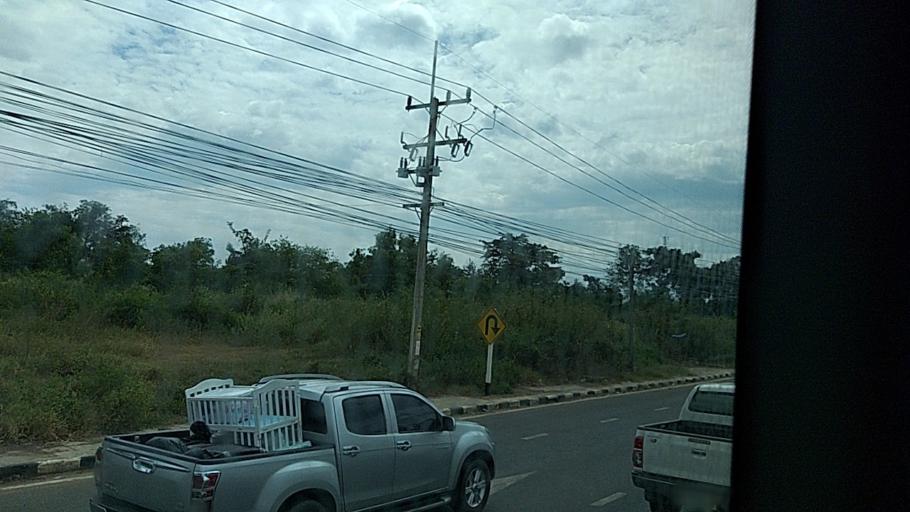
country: TH
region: Maha Sarakham
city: Maha Sarakham
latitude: 16.2453
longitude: 103.2728
